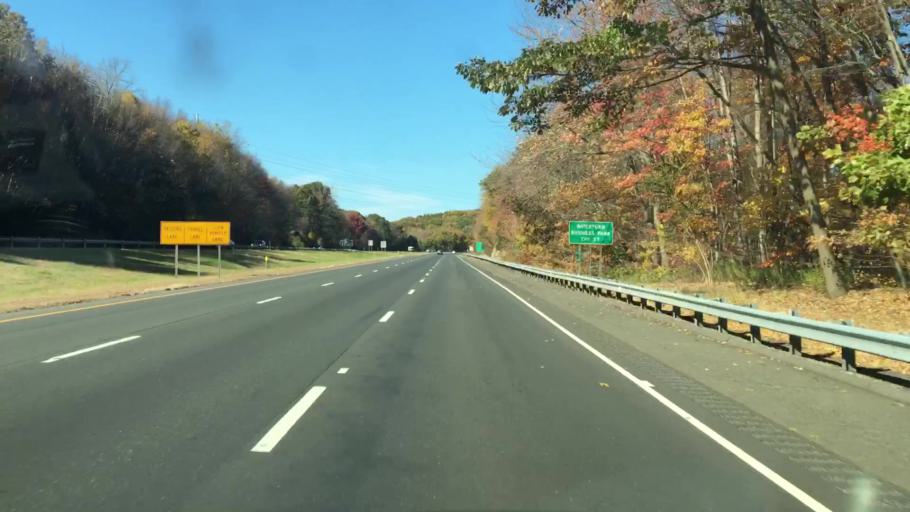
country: US
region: Connecticut
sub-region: Litchfield County
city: Oakville
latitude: 41.5935
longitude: -73.0622
